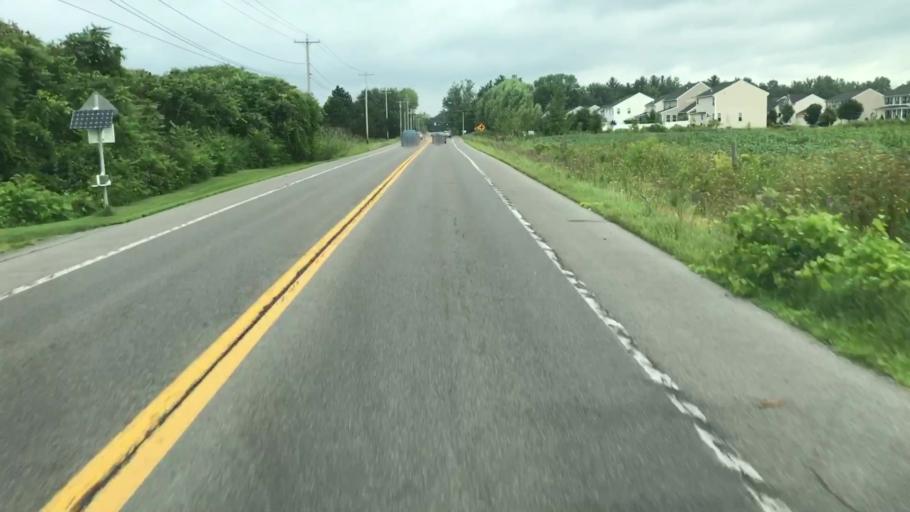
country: US
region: New York
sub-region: Onondaga County
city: Liverpool
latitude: 43.1654
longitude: -76.2087
